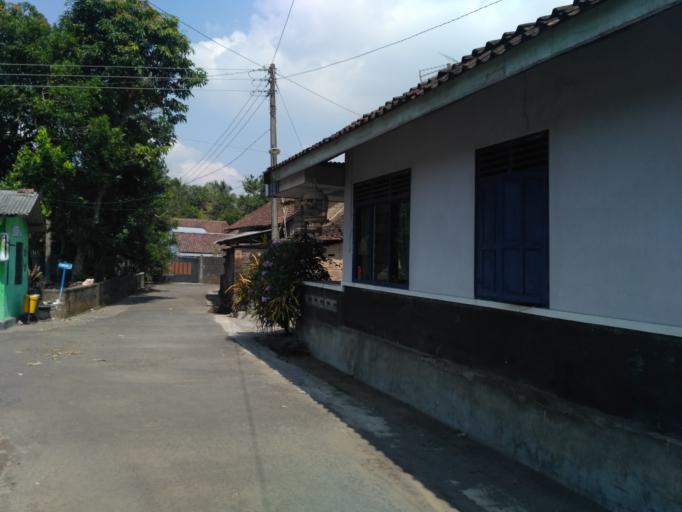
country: ID
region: Daerah Istimewa Yogyakarta
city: Depok
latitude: -7.7084
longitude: 110.4174
